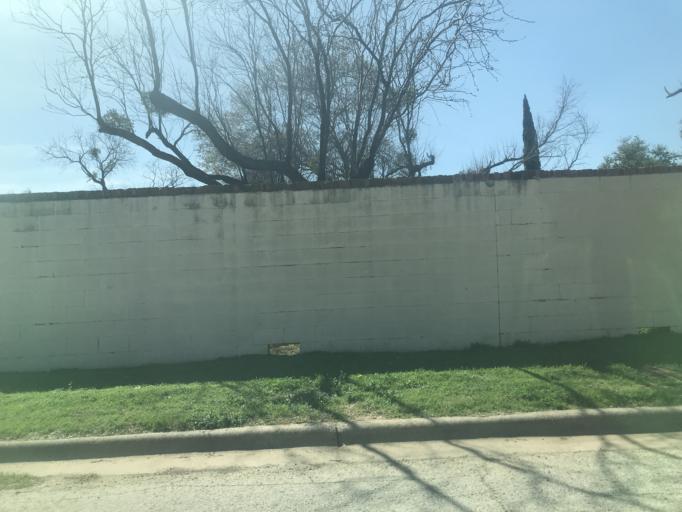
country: US
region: Texas
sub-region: Taylor County
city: Abilene
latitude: 32.4491
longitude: -99.7675
